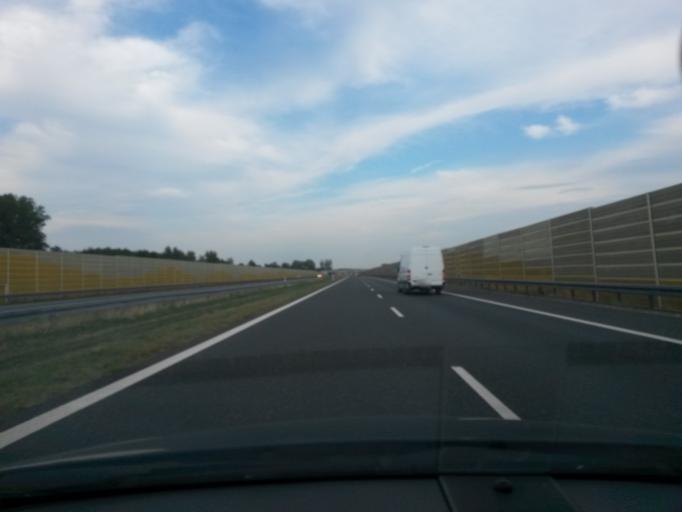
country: PL
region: Lodz Voivodeship
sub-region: Powiat leczycki
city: Swinice Warckie
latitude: 52.0304
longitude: 18.8950
